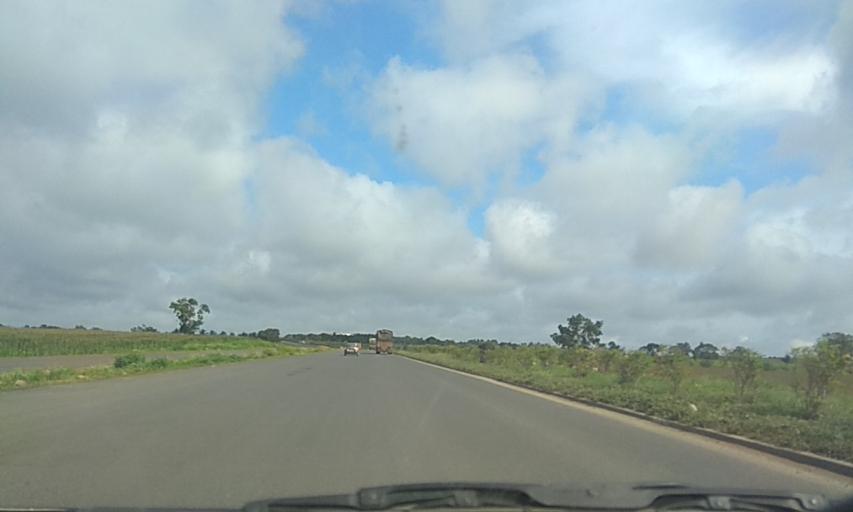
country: IN
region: Karnataka
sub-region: Haveri
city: Shiggaon
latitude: 15.0023
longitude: 75.2058
